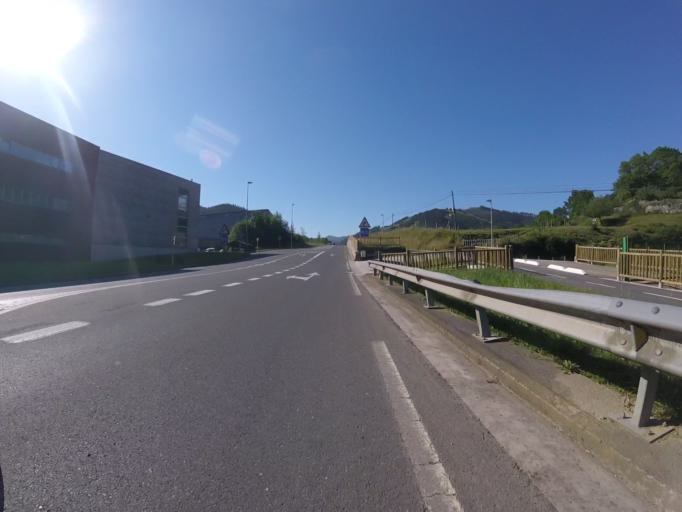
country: ES
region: Basque Country
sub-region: Provincia de Guipuzcoa
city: Azpeitia
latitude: 43.1631
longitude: -2.2463
